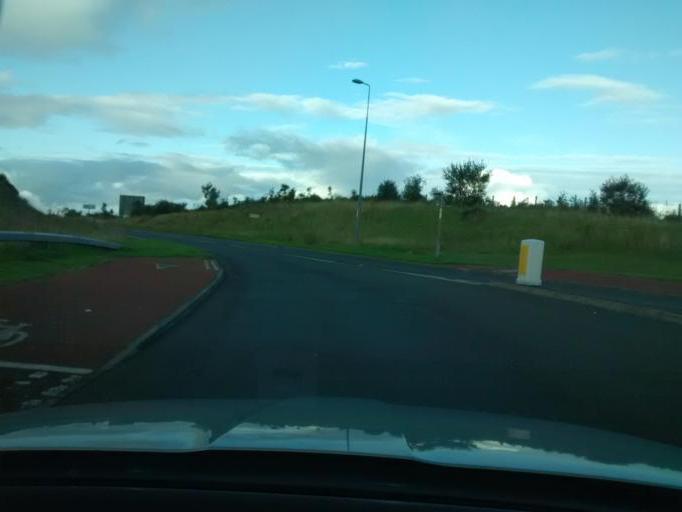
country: GB
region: Scotland
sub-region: North Ayrshire
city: Saltcoats
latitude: 55.6552
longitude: -4.7733
